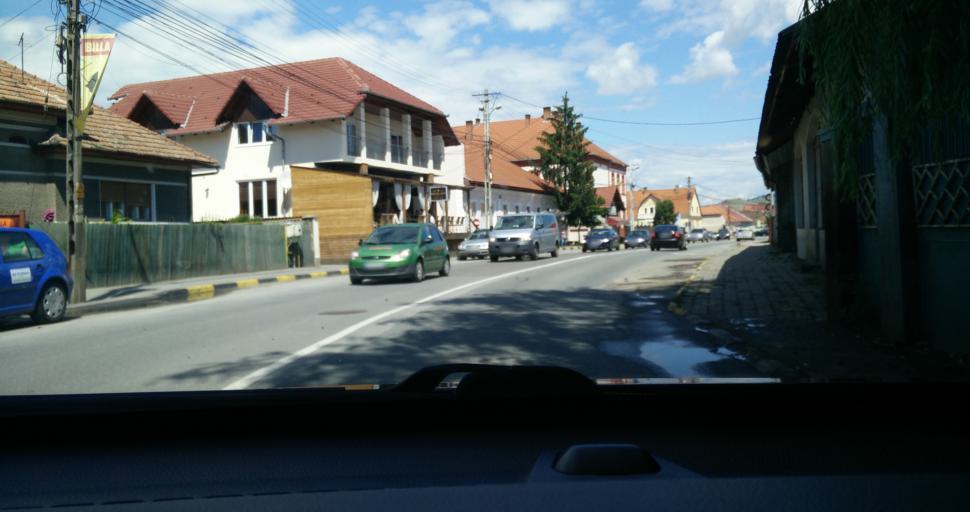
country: RO
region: Alba
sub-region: Municipiul Sebes
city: Sebes
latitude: 45.9564
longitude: 23.5651
